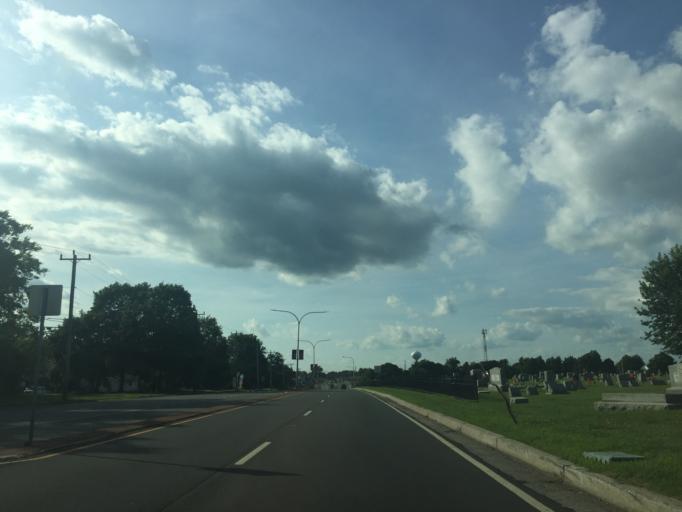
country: US
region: Delaware
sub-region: Kent County
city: Smyrna
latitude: 39.2936
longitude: -75.5977
